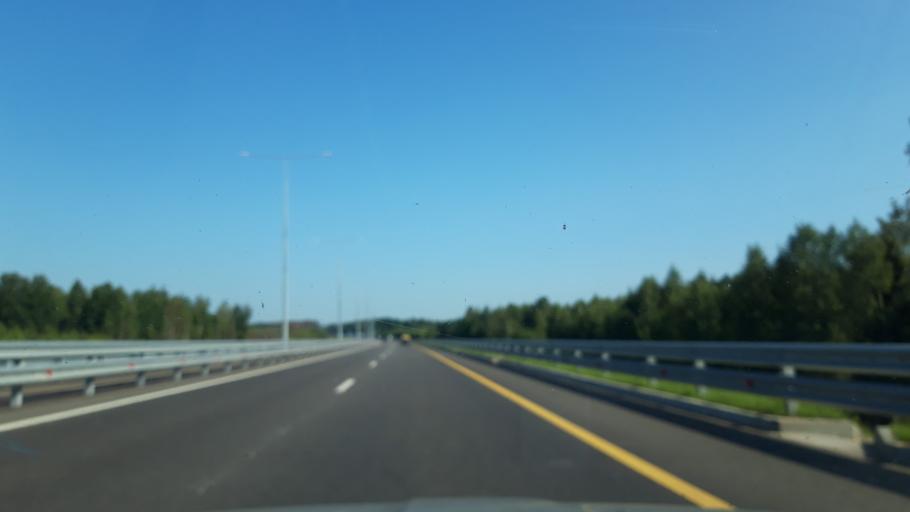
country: RU
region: Moskovskaya
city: Spas-Zaulok
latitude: 56.4743
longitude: 36.5402
